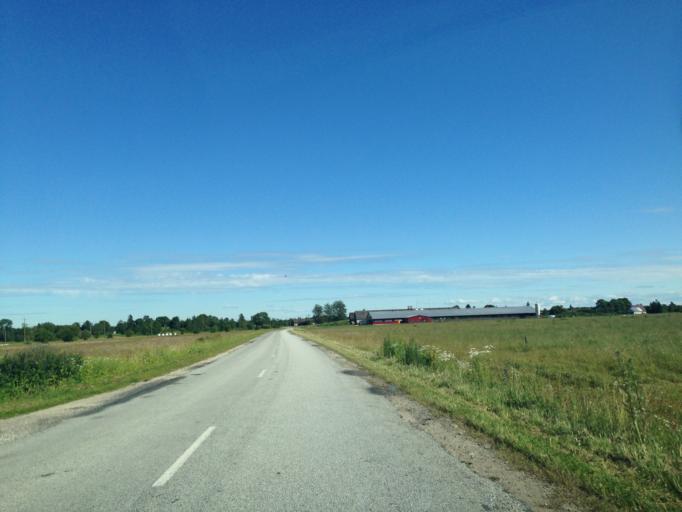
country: EE
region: Harju
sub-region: Kuusalu vald
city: Kuusalu
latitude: 59.4604
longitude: 25.3403
